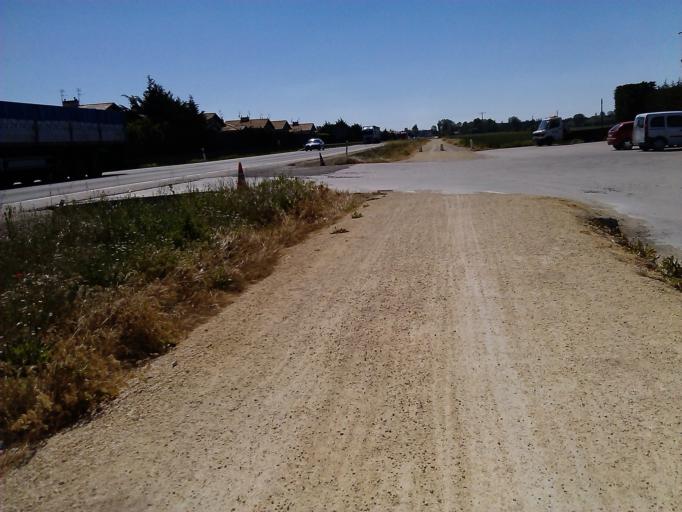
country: ES
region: Castille and Leon
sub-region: Provincia de Burgos
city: Ibeas de Juarros
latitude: 42.3325
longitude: -3.5475
